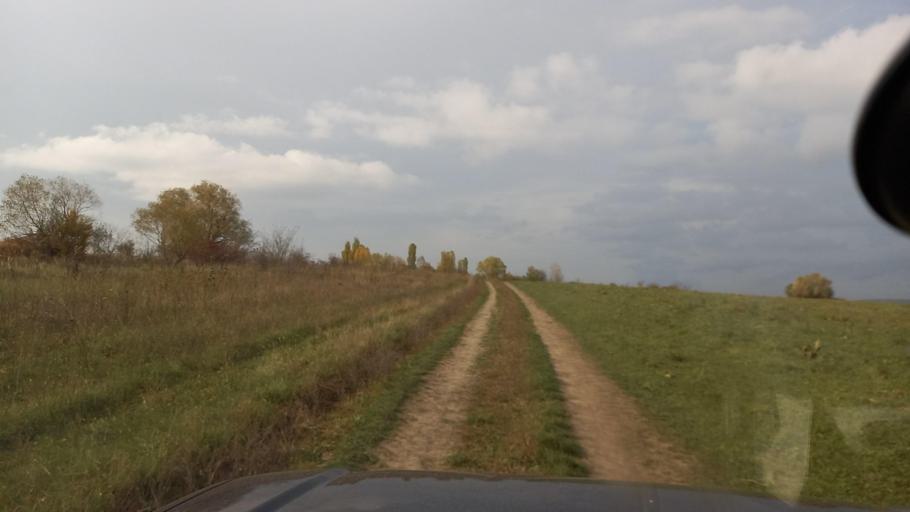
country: RU
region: Krasnodarskiy
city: Gubskaya
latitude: 44.3059
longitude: 40.5513
